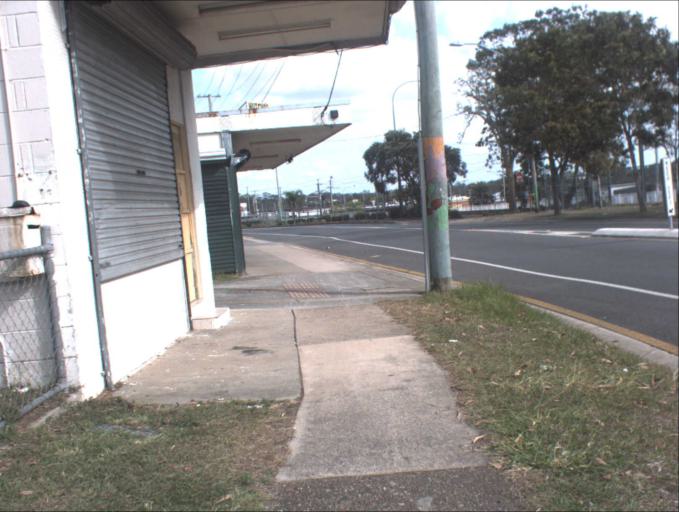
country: AU
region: Queensland
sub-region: Logan
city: Logan City
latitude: -27.6396
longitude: 153.1054
